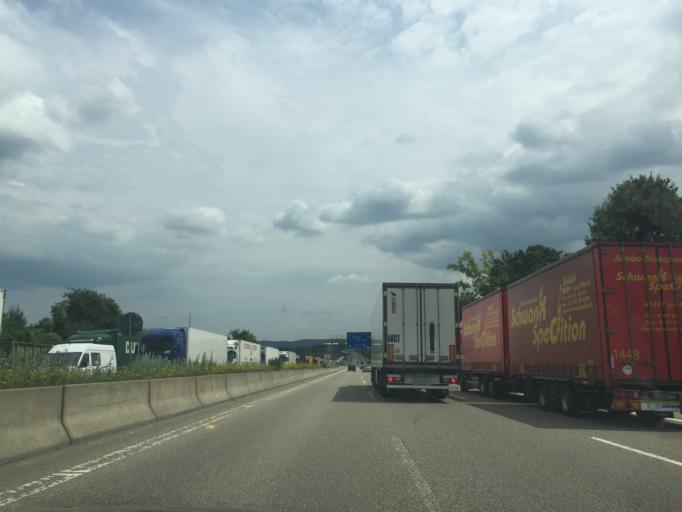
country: DE
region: Baden-Wuerttemberg
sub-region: Karlsruhe Region
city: Sinsheim
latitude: 49.2517
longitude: 8.8488
